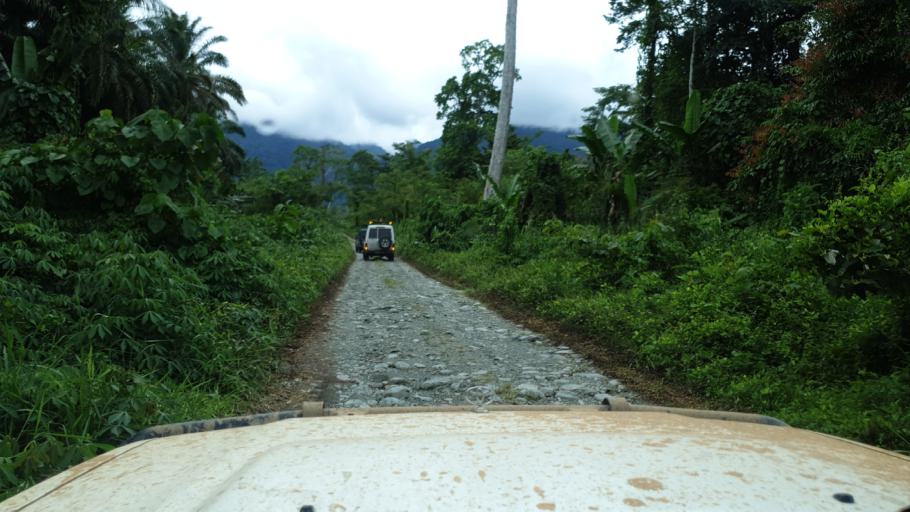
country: PG
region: Northern Province
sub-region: Sohe
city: Kokoda
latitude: -8.9355
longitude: 147.8675
